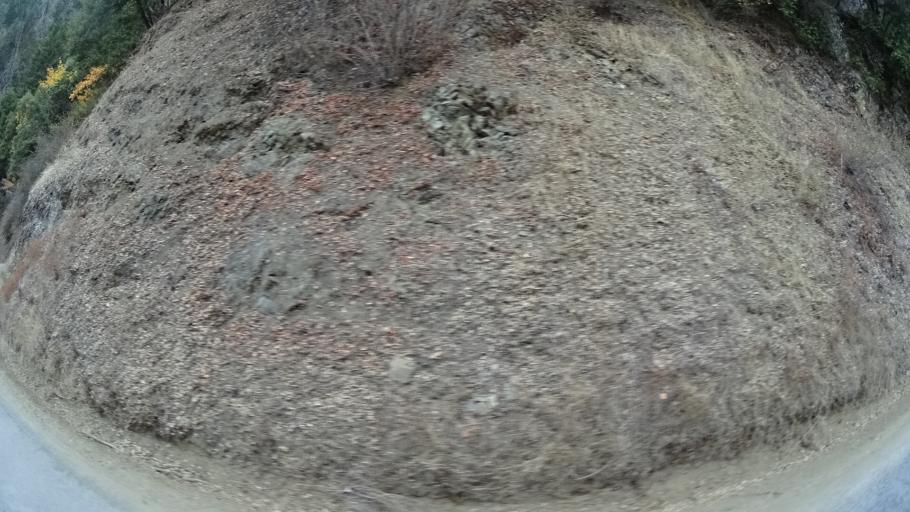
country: US
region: California
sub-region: Siskiyou County
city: Happy Camp
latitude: 41.7762
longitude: -123.3486
